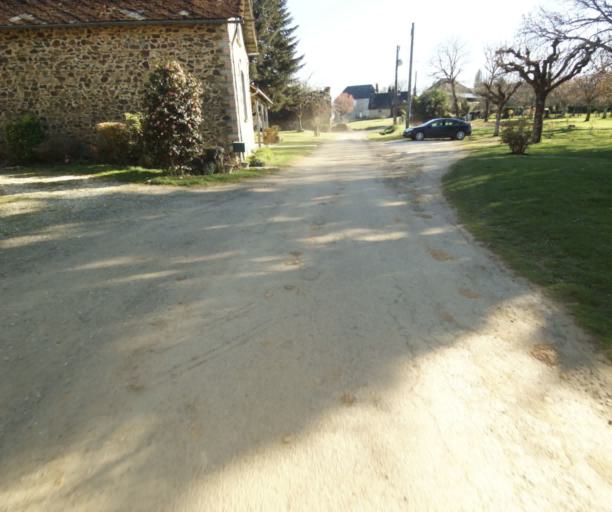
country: FR
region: Limousin
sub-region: Departement de la Correze
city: Seilhac
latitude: 45.3861
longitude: 1.7350
